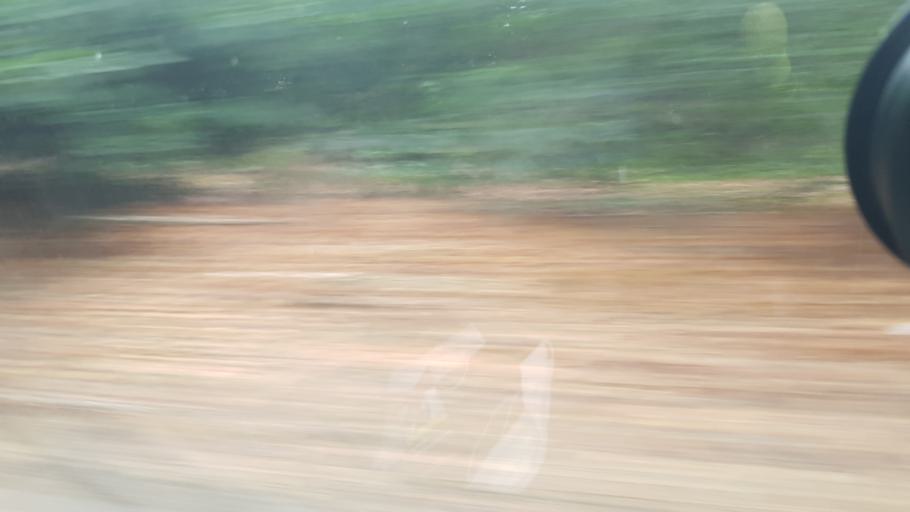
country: GB
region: England
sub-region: Hampshire
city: Yateley
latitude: 51.3156
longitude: -0.8173
